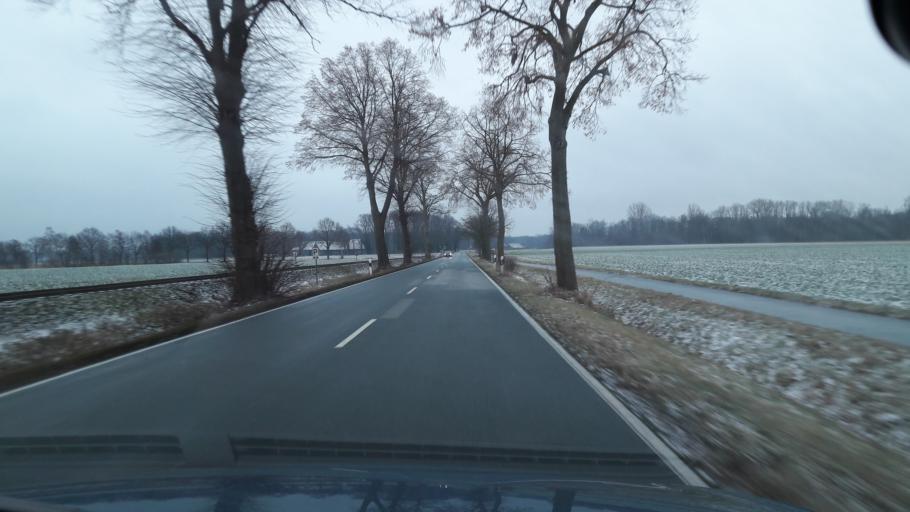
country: DE
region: North Rhine-Westphalia
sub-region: Regierungsbezirk Munster
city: Wadersloh
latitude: 51.6949
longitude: 8.2775
